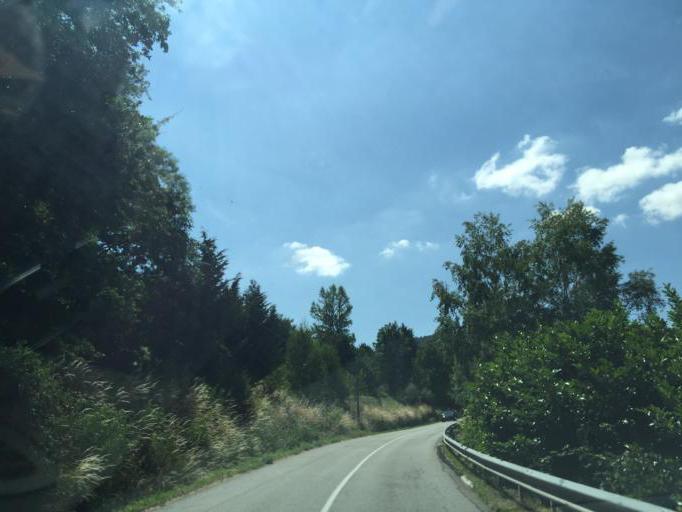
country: FR
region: Rhone-Alpes
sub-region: Departement de la Loire
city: Saint-Chamond
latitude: 45.4127
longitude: 4.5187
